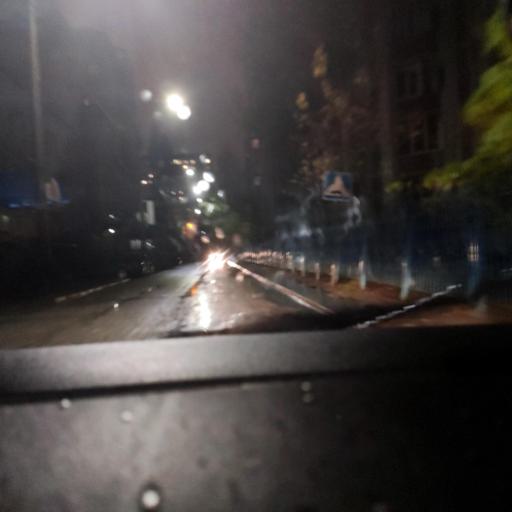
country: RU
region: Voronezj
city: Podgornoye
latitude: 51.7104
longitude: 39.1690
